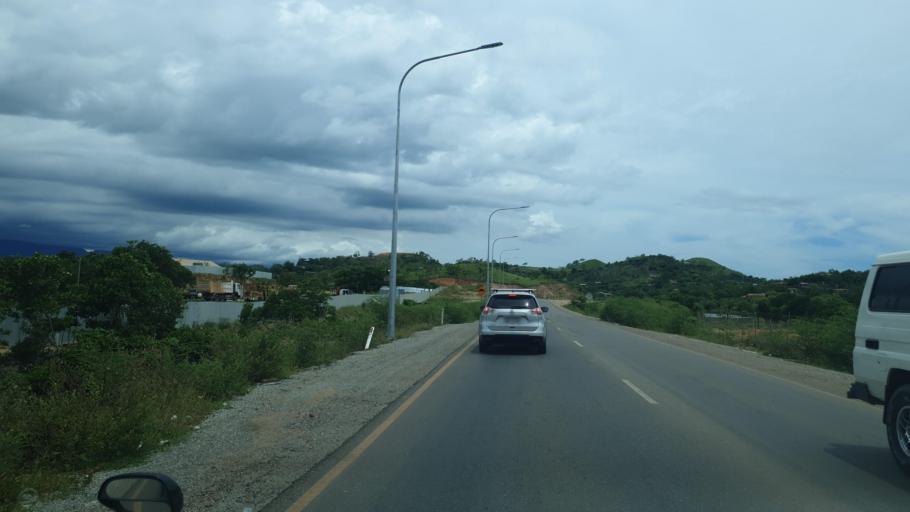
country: PG
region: National Capital
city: Port Moresby
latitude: -9.5048
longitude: 147.2367
